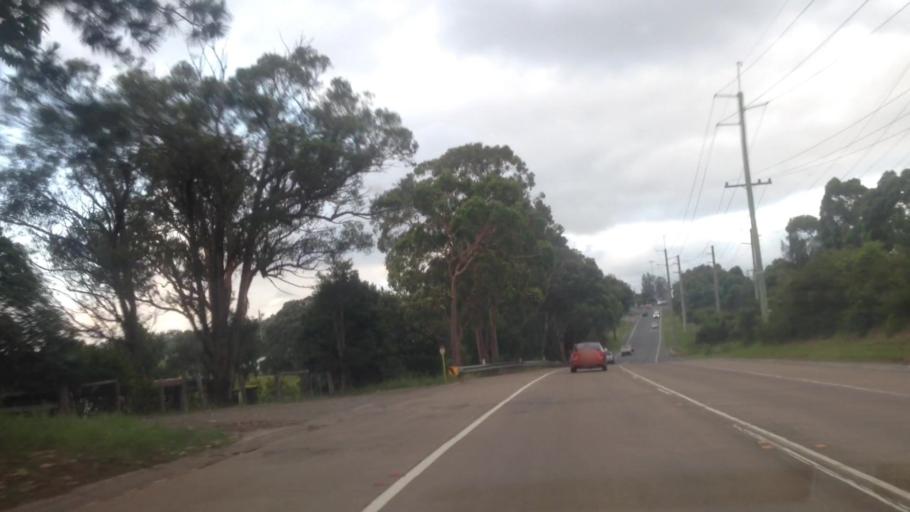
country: AU
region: New South Wales
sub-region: Lake Macquarie Shire
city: Dora Creek
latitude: -33.1147
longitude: 151.4726
